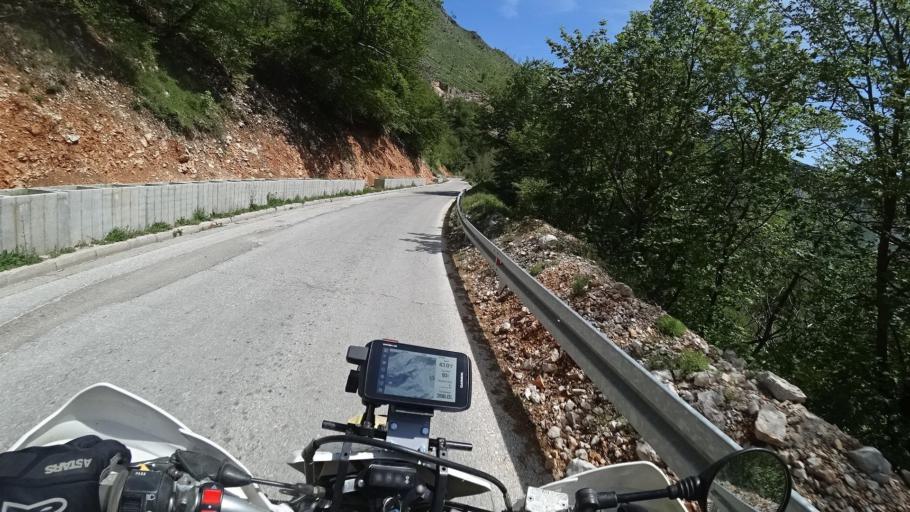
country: BA
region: Federation of Bosnia and Herzegovina
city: Potoci
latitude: 43.4600
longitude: 17.9563
